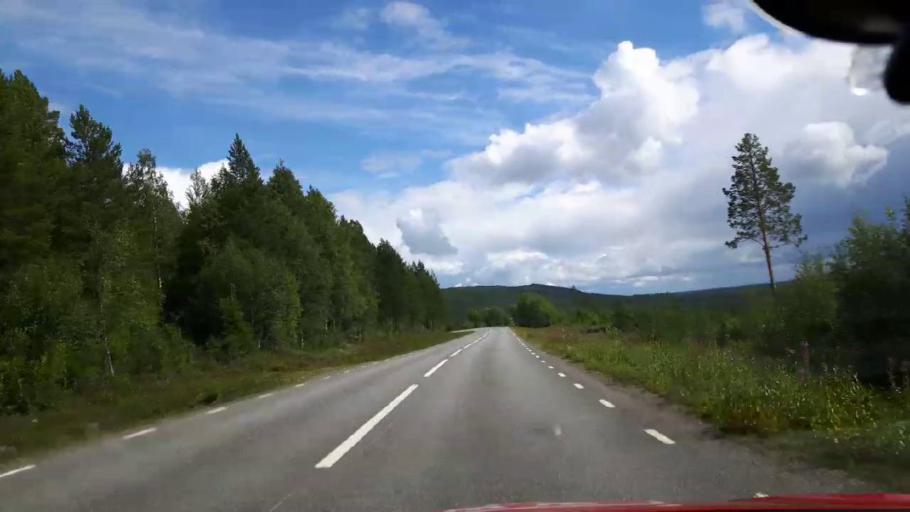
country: SE
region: Jaemtland
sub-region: Stroemsunds Kommun
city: Stroemsund
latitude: 64.3428
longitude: 15.1239
